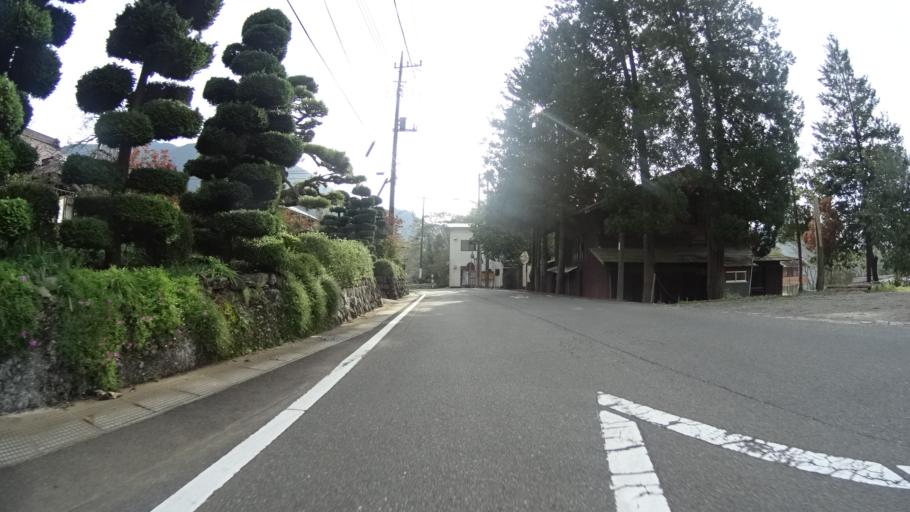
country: JP
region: Yamanashi
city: Uenohara
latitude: 35.6748
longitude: 139.0892
